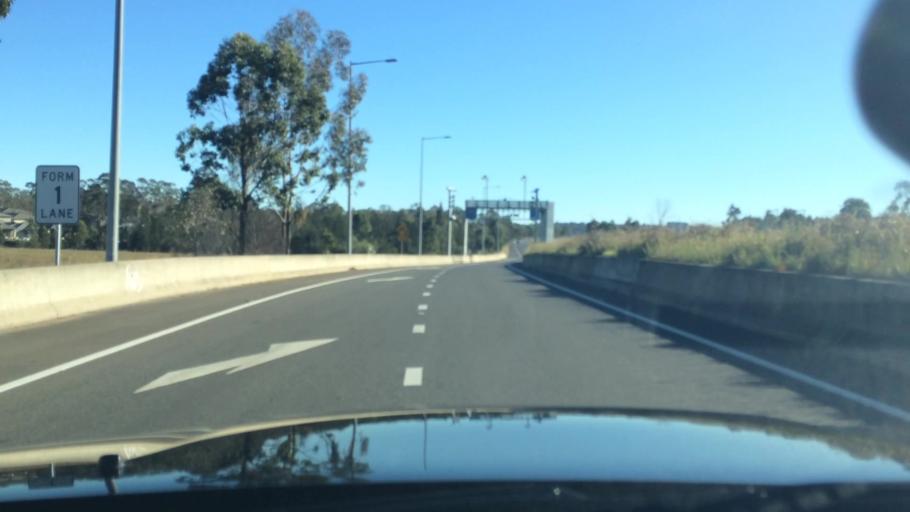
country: AU
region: New South Wales
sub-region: Liverpool
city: Miller
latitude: -33.9174
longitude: 150.8515
